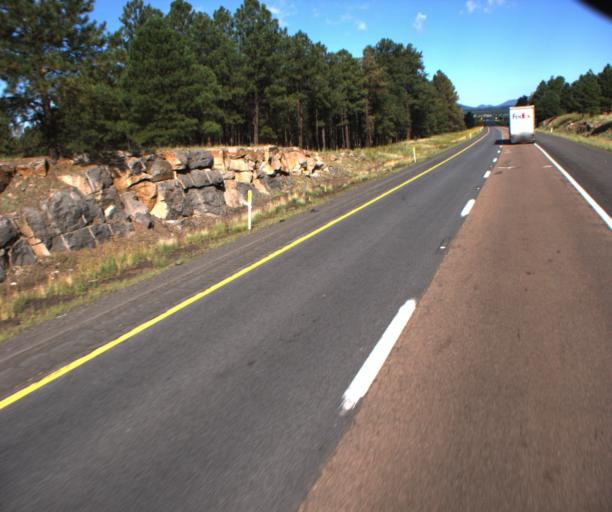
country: US
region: Arizona
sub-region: Coconino County
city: Flagstaff
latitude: 35.2243
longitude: -111.7969
